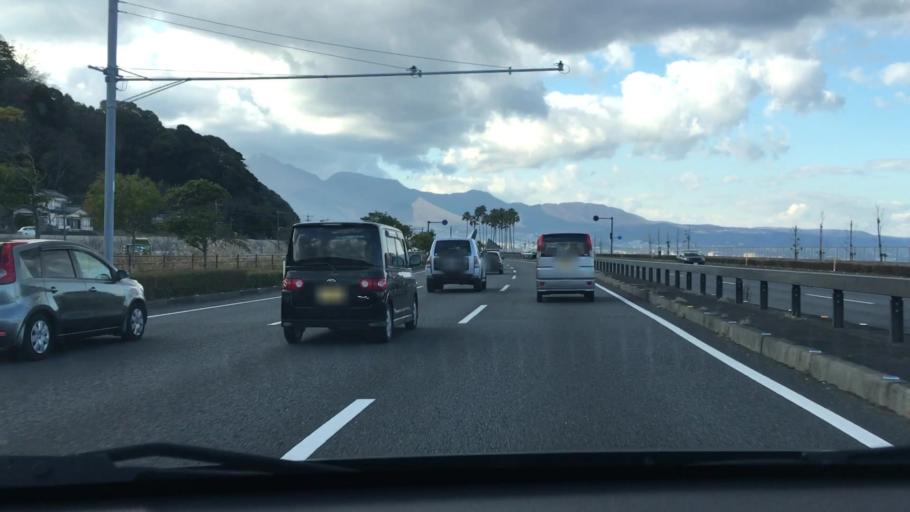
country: JP
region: Oita
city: Oita
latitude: 33.2542
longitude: 131.5628
